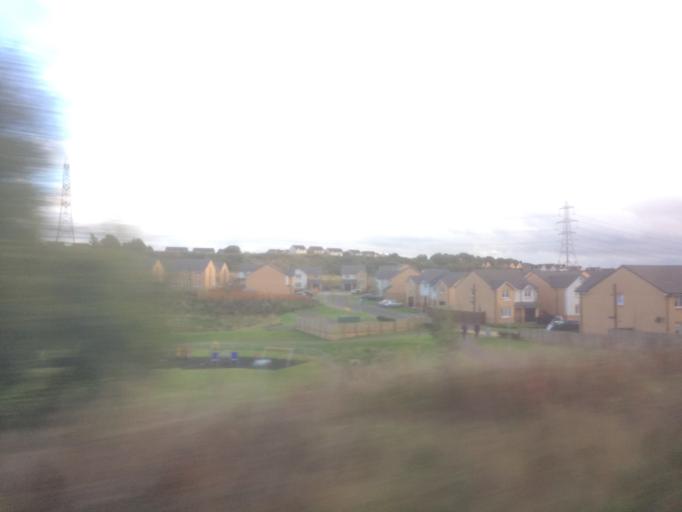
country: GB
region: Scotland
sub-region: North Lanarkshire
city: Kilsyth
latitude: 55.9548
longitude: -4.0378
